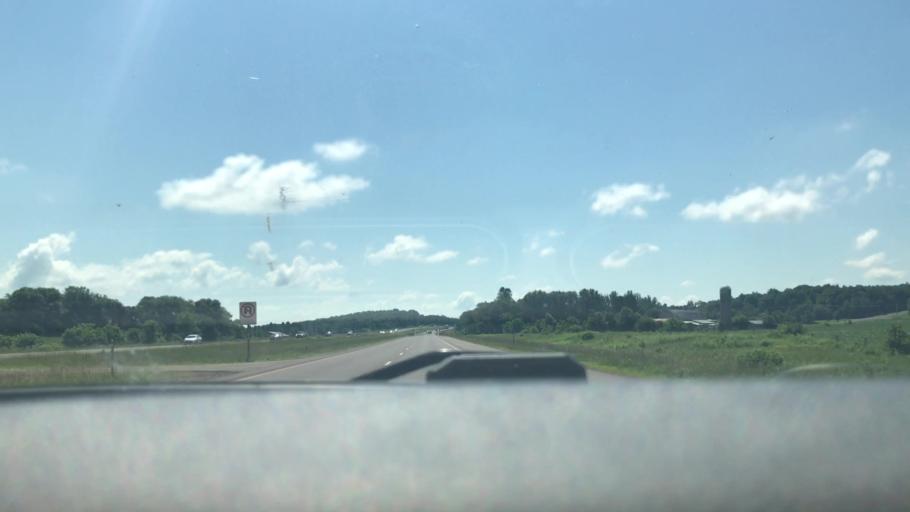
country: US
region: Wisconsin
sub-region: Chippewa County
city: Bloomer
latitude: 45.0950
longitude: -91.4975
